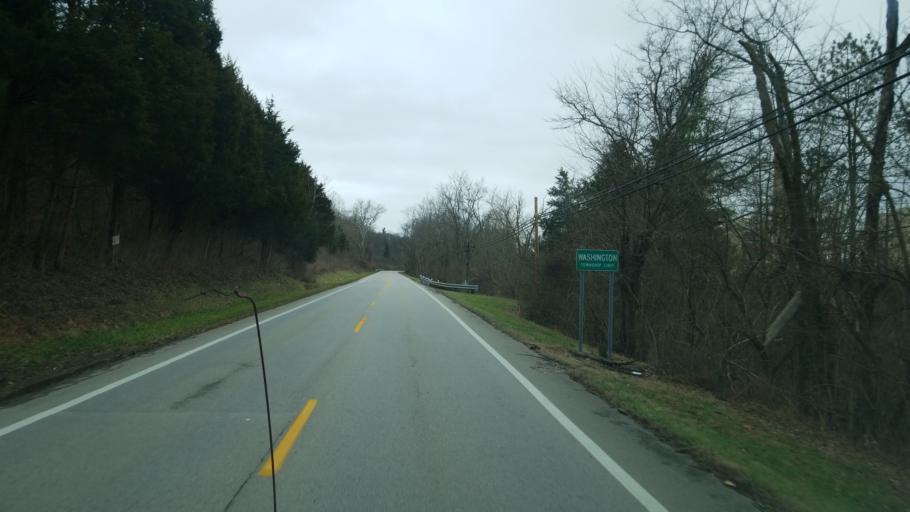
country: US
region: Ohio
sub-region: Clermont County
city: New Richmond
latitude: 38.8763
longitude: -84.2259
